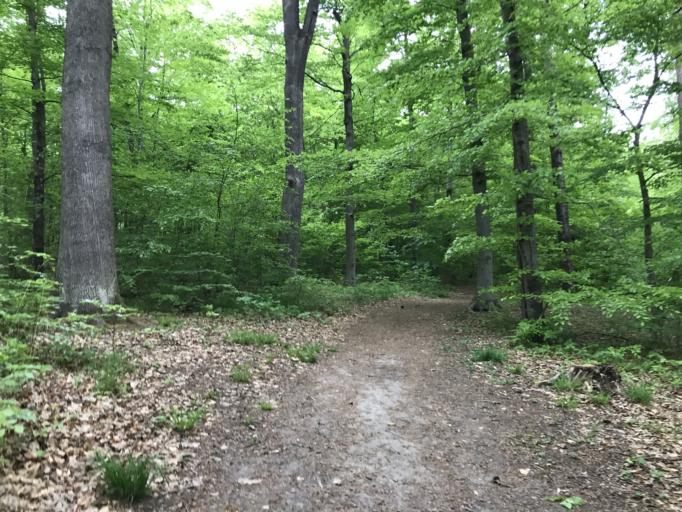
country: DE
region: Baden-Wuerttemberg
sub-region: Regierungsbezirk Stuttgart
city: Stuttgart
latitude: 48.7436
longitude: 9.1212
